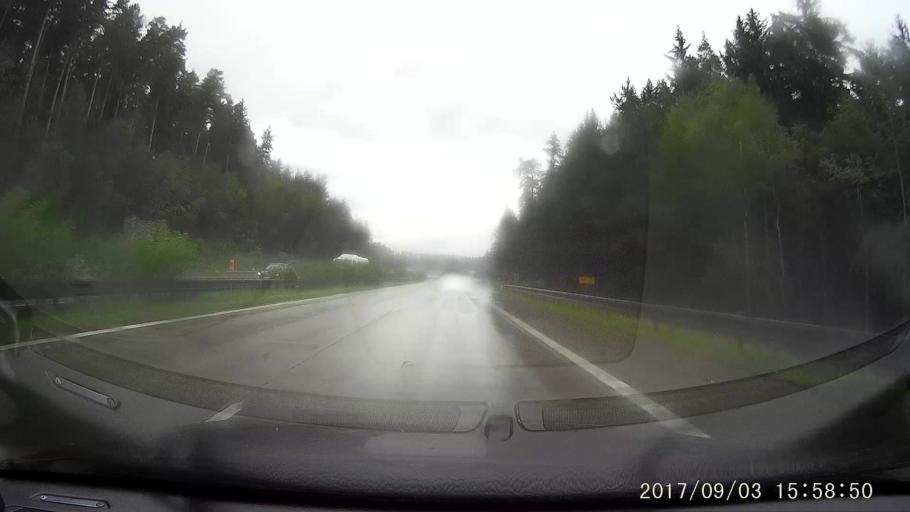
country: CZ
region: Vysocina
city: Heralec
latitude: 49.5107
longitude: 15.4629
